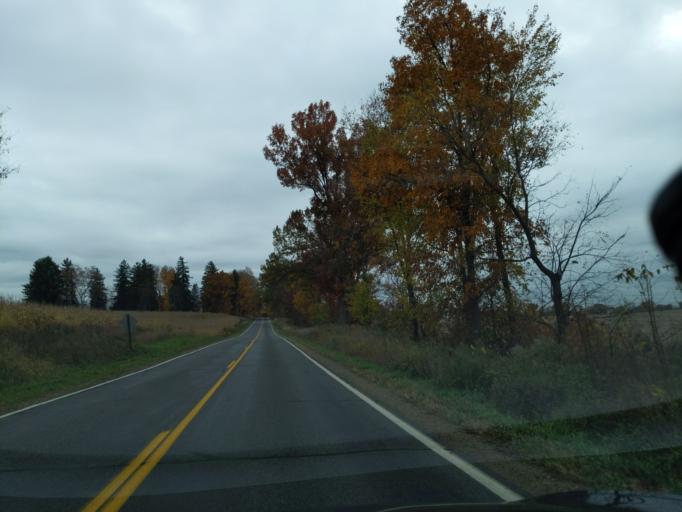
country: US
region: Michigan
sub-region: Jackson County
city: Spring Arbor
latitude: 42.3479
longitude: -84.6005
